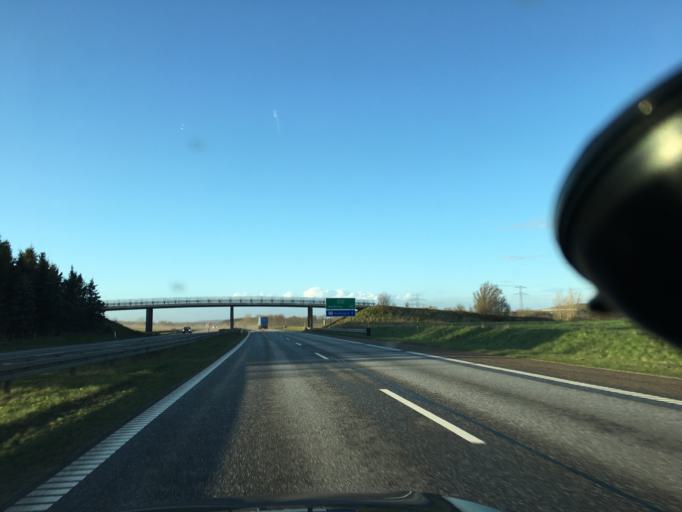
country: DK
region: North Denmark
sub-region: Alborg Kommune
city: Svenstrup
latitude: 56.9643
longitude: 9.8761
